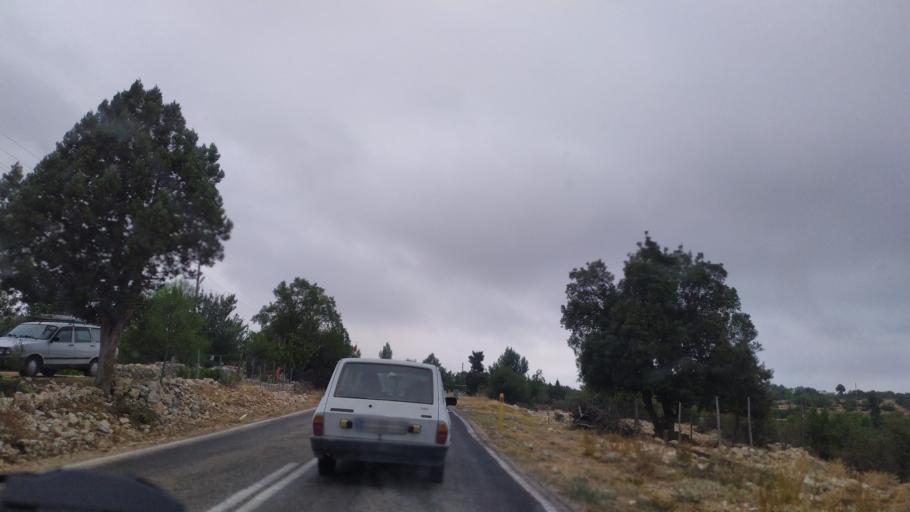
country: TR
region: Mersin
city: Silifke
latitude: 36.5485
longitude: 33.9214
